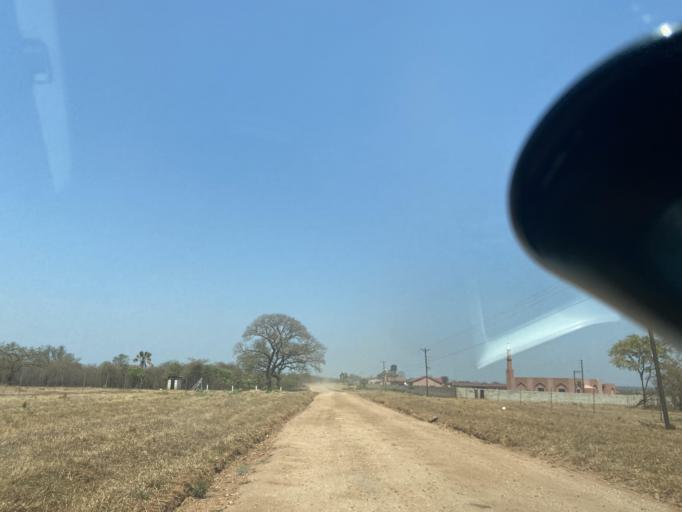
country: ZM
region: Lusaka
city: Lusaka
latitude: -15.5221
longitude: 28.1113
